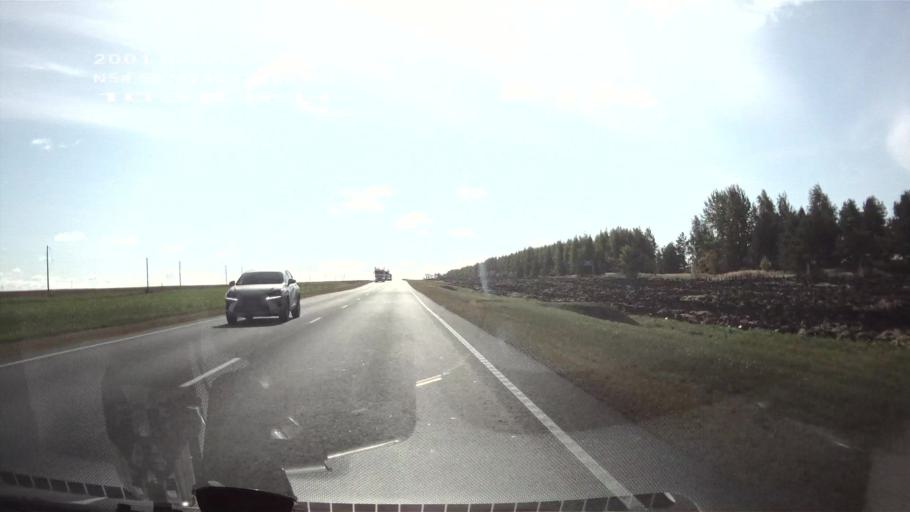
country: RU
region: Ulyanovsk
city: Tsil'na
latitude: 54.5871
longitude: 47.8815
